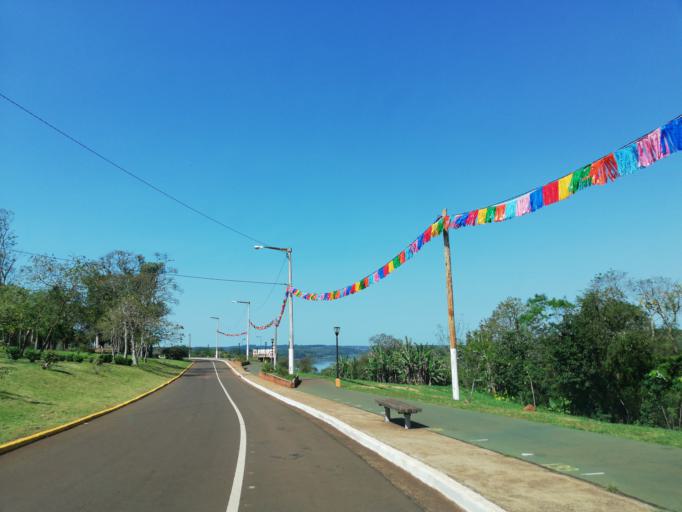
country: AR
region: Misiones
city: Puerto Eldorado
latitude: -26.4123
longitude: -54.6935
